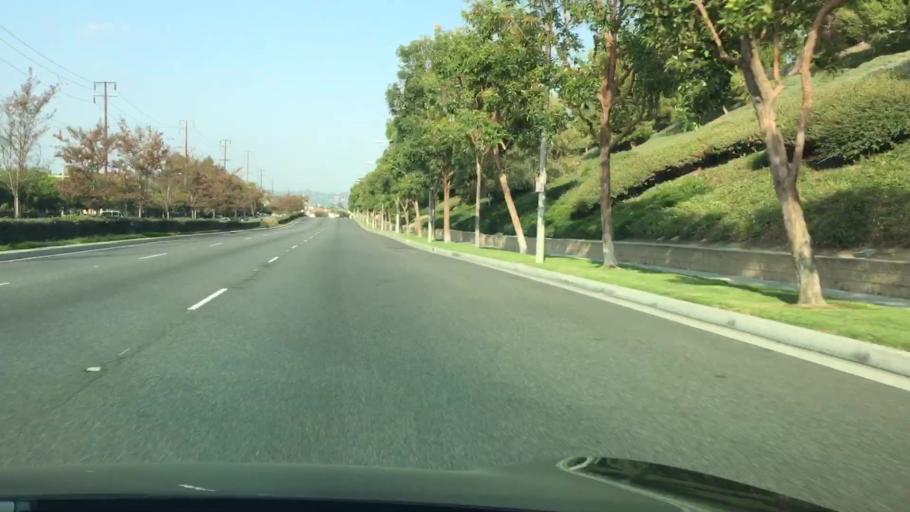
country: US
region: California
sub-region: Los Angeles County
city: East La Mirada
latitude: 33.9054
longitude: -117.9805
